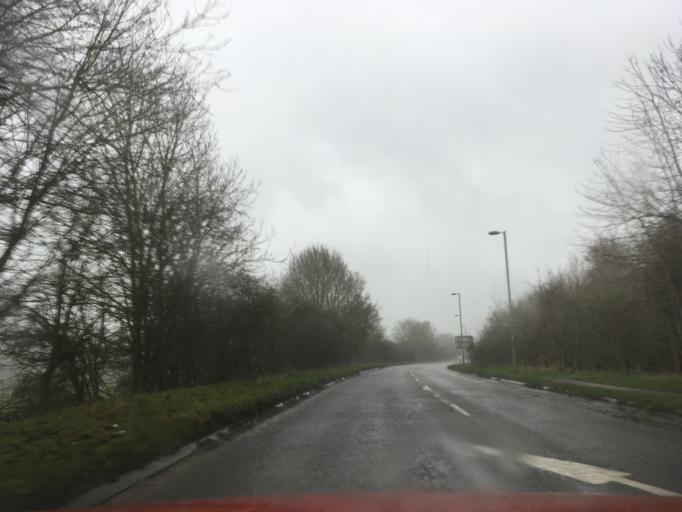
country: GB
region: England
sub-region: Oxfordshire
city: Eynsham
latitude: 51.7829
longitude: -1.3655
